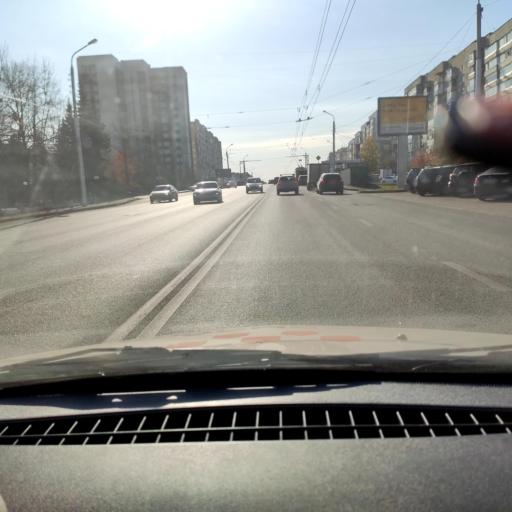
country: RU
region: Bashkortostan
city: Ufa
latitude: 54.7104
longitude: 56.0005
